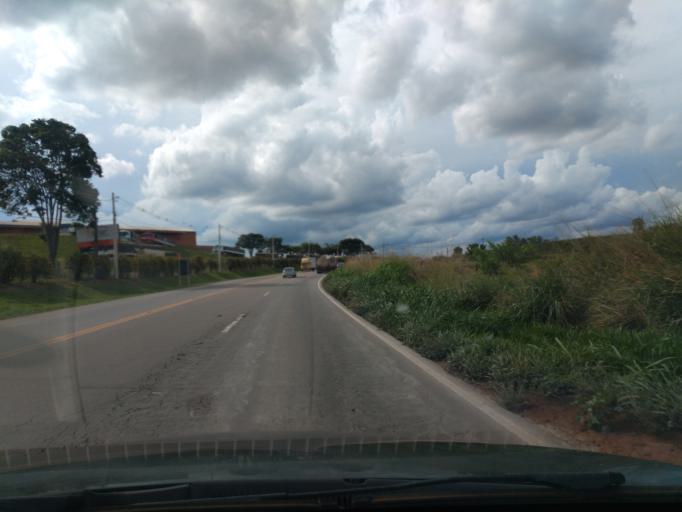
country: BR
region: Minas Gerais
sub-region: Varginha
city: Varginha
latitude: -21.6008
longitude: -45.4376
